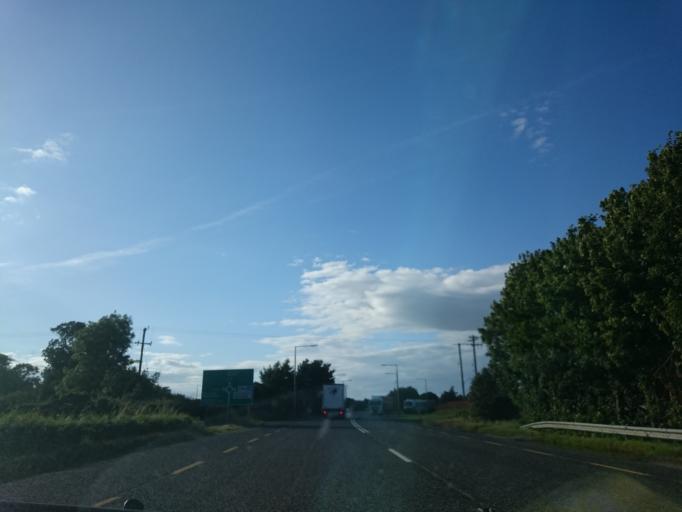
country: IE
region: Leinster
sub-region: Loch Garman
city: Loch Garman
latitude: 52.3363
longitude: -6.5145
